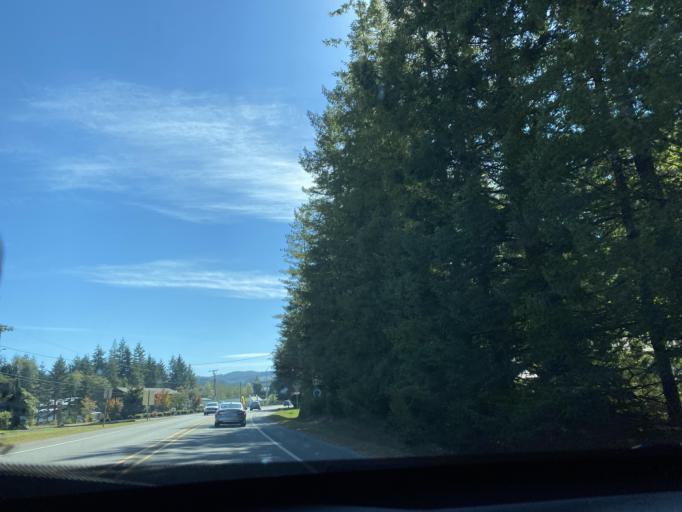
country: US
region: Washington
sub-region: Clallam County
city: Forks
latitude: 47.9554
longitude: -124.3861
